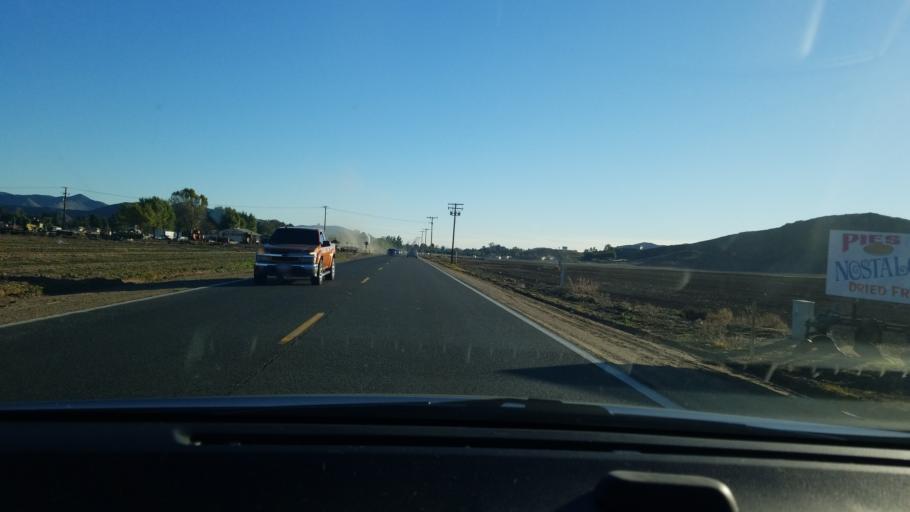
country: US
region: California
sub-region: Riverside County
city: Green Acres
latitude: 33.7248
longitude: -117.0764
